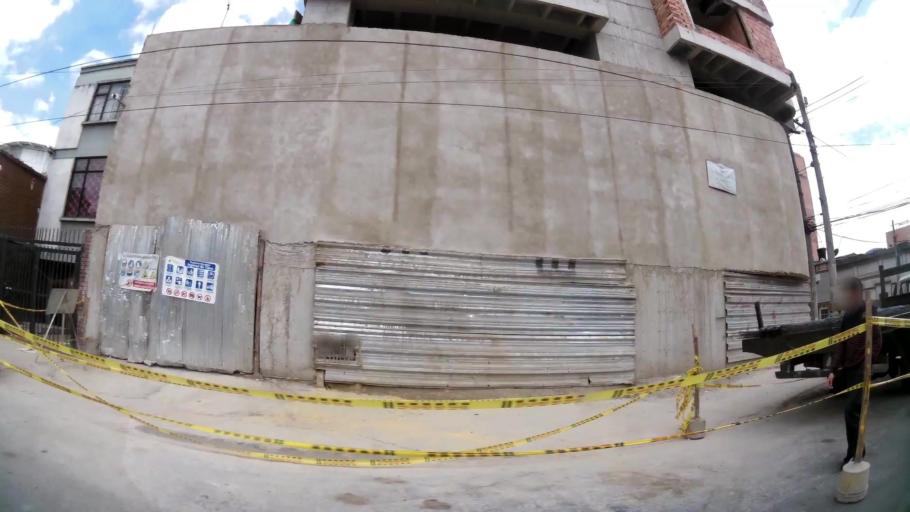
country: CO
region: Bogota D.C.
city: Bogota
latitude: 4.6390
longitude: -74.0751
